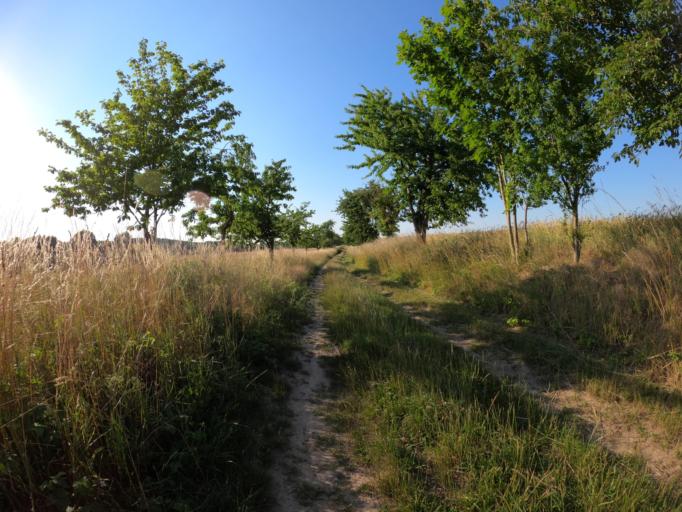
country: DE
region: Brandenburg
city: Tantow
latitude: 53.2447
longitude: 14.3676
